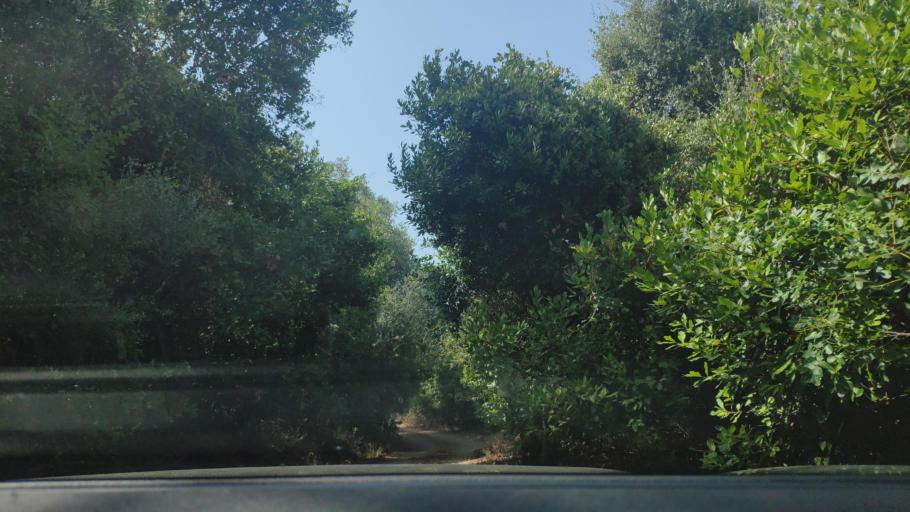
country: GR
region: West Greece
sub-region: Nomos Aitolias kai Akarnanias
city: Fitiai
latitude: 38.7335
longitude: 21.1824
